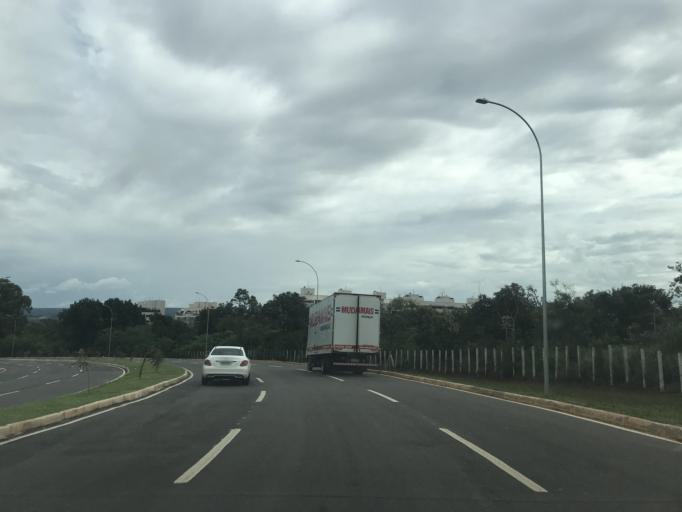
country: BR
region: Federal District
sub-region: Brasilia
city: Brasilia
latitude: -15.7506
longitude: -47.9138
